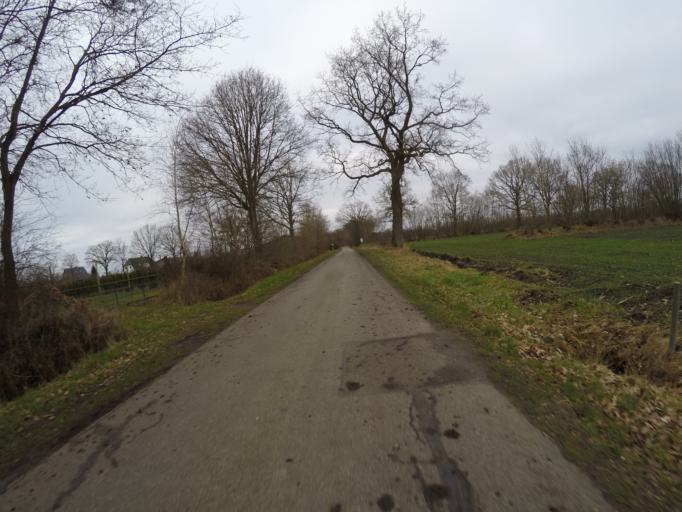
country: DE
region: Schleswig-Holstein
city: Hemdingen
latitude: 53.7711
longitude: 9.8431
